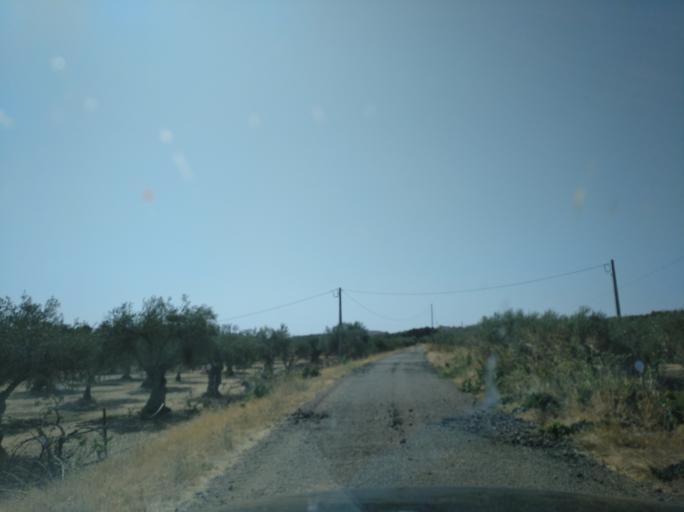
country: PT
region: Portalegre
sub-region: Campo Maior
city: Campo Maior
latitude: 39.0740
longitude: -7.0173
